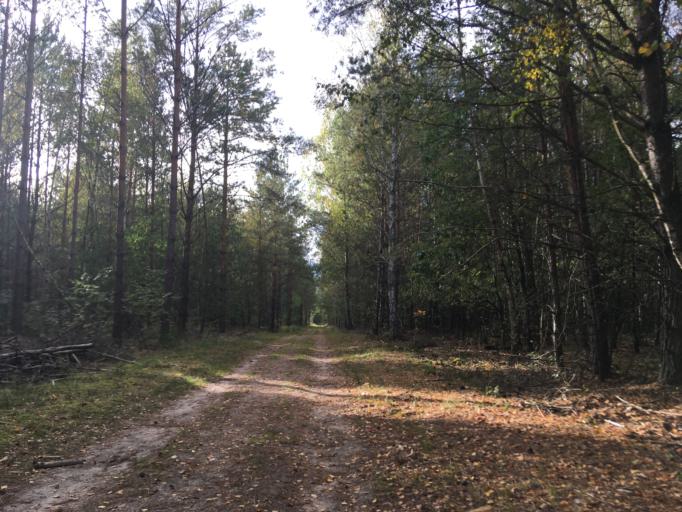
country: DE
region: Brandenburg
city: Glienicke
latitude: 52.6981
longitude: 13.3571
